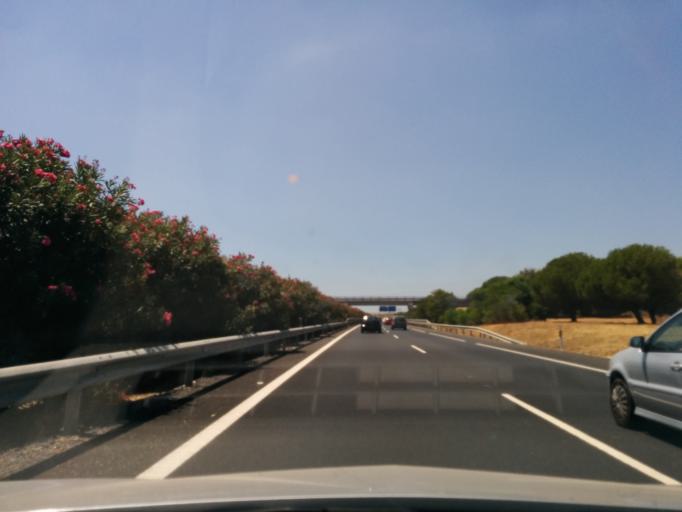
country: ES
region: Andalusia
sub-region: Provincia de Huelva
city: San Juan del Puerto
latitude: 37.3198
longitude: -6.8530
